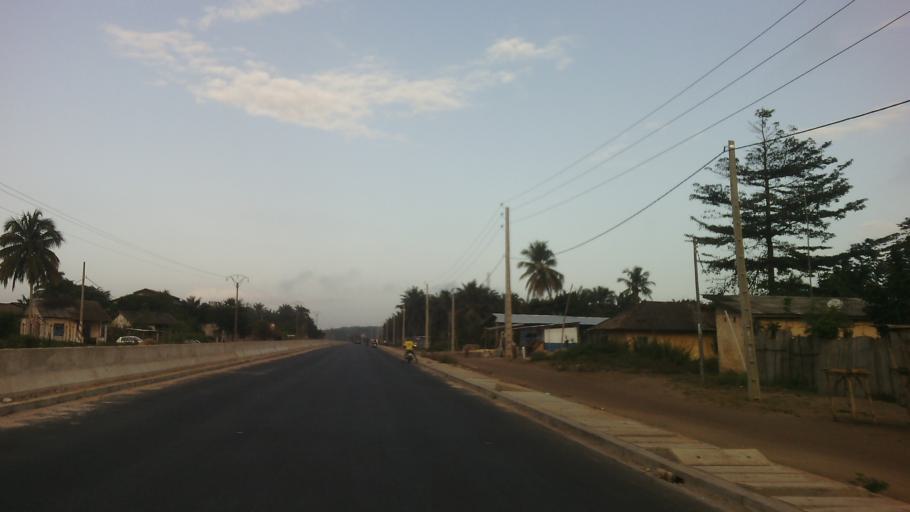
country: BJ
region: Atlantique
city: Hevie
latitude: 6.3825
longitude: 2.1780
